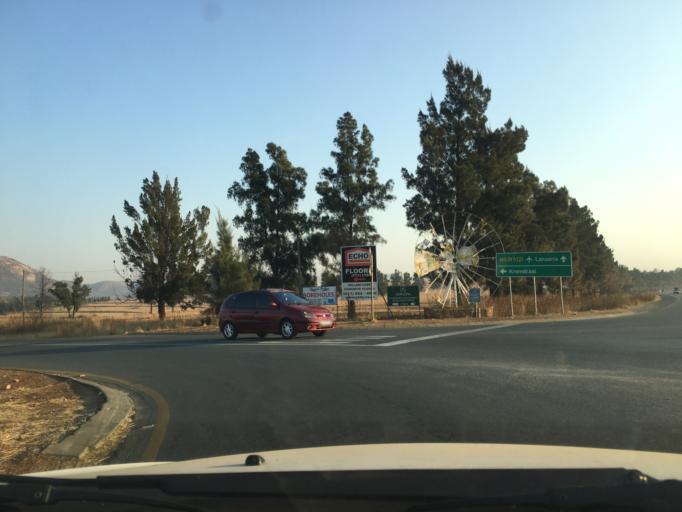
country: ZA
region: Gauteng
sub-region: West Rand District Municipality
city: Muldersdriseloop
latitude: -25.9946
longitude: 27.8574
